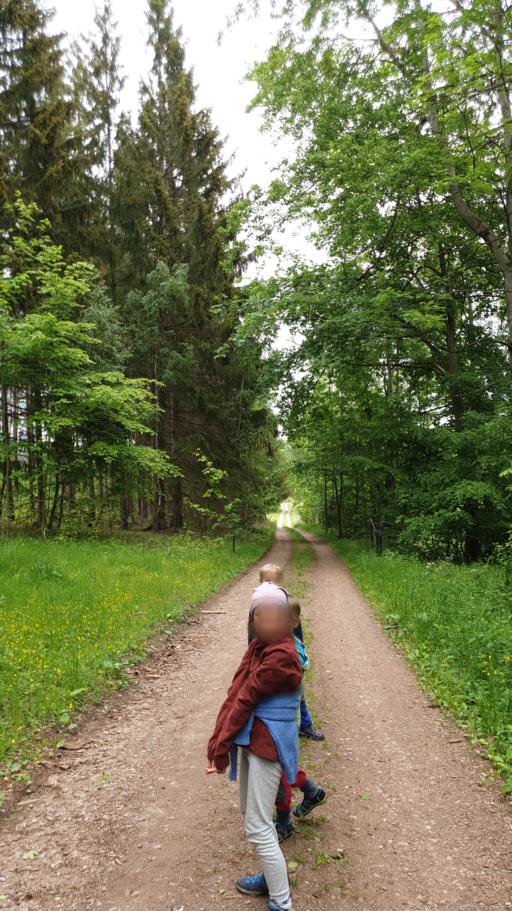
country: DE
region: Saxony
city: Barenstein
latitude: 50.8058
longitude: 13.7705
